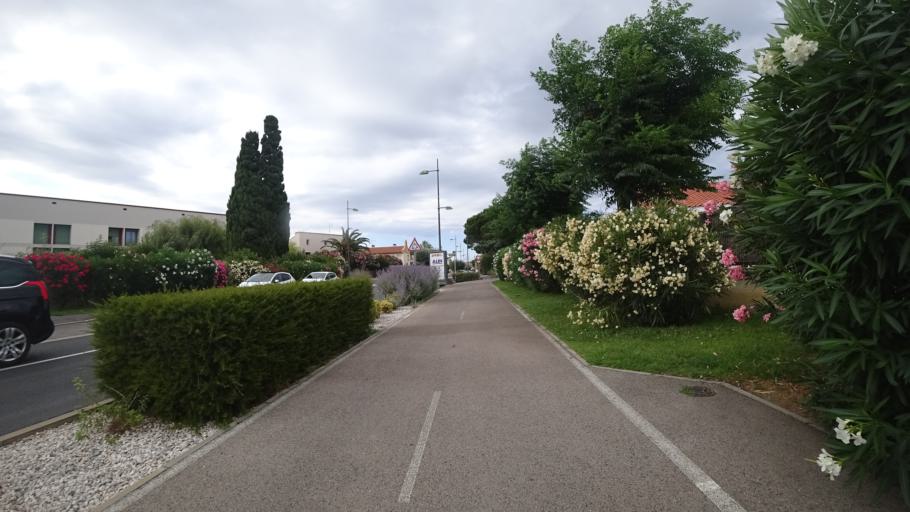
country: FR
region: Languedoc-Roussillon
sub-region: Departement des Pyrenees-Orientales
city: Saint-Laurent-de-la-Salanque
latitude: 42.7671
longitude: 2.9871
